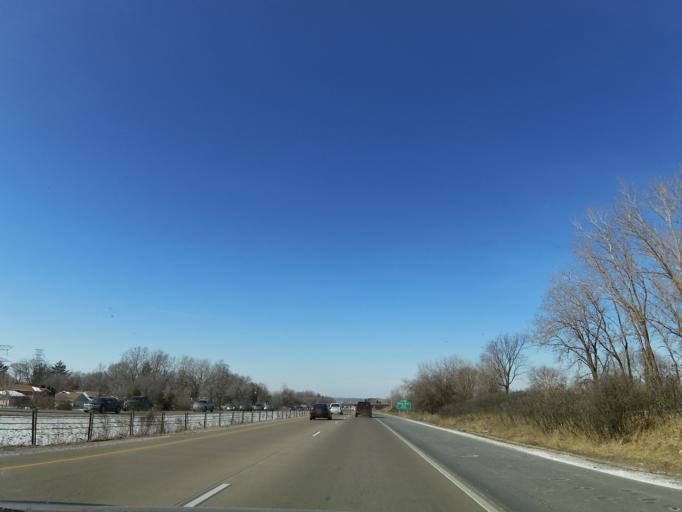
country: US
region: Minnesota
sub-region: Ramsey County
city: North Saint Paul
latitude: 45.0359
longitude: -92.9975
